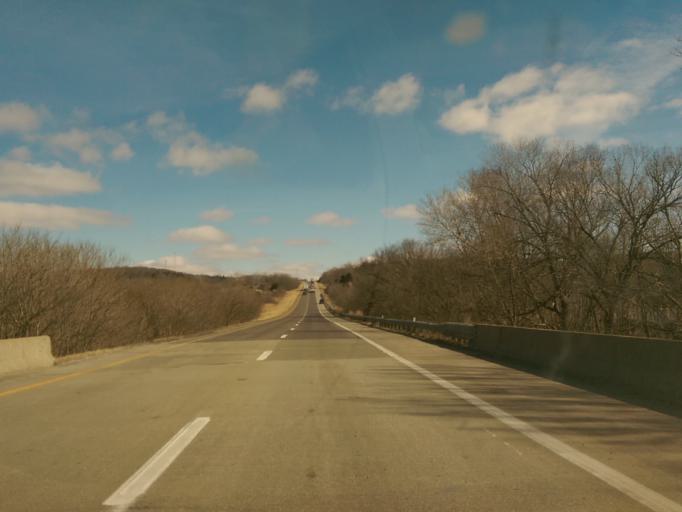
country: US
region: Missouri
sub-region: Montgomery County
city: Montgomery City
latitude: 38.9003
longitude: -91.5806
